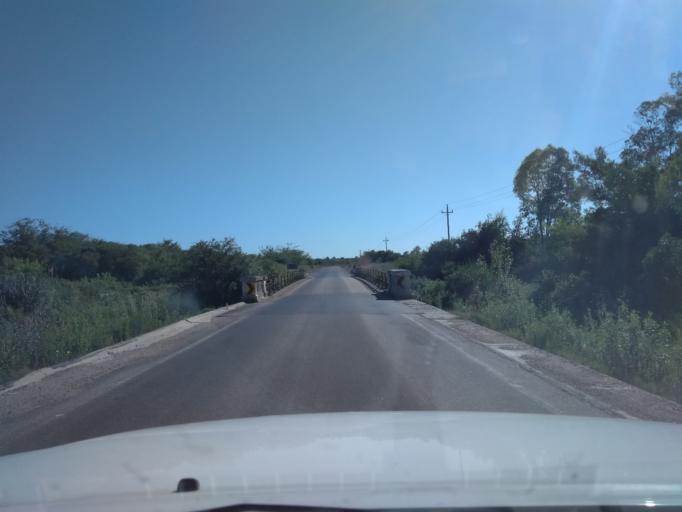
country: UY
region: Canelones
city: San Ramon
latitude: -34.2708
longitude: -55.9425
